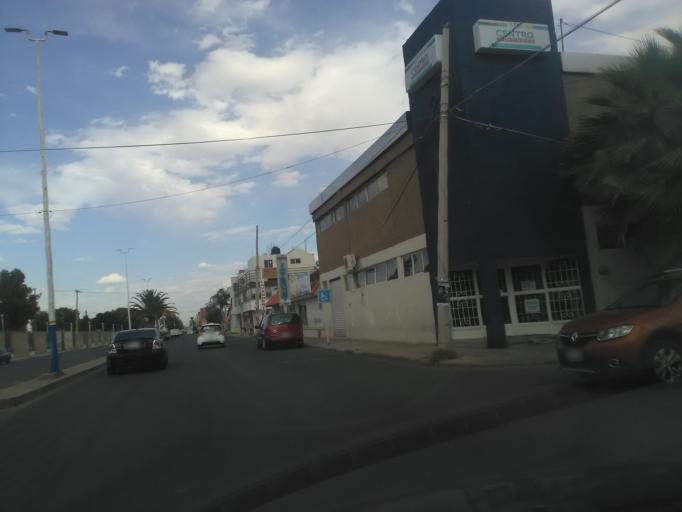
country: MX
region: Durango
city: Victoria de Durango
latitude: 24.0198
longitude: -104.6391
